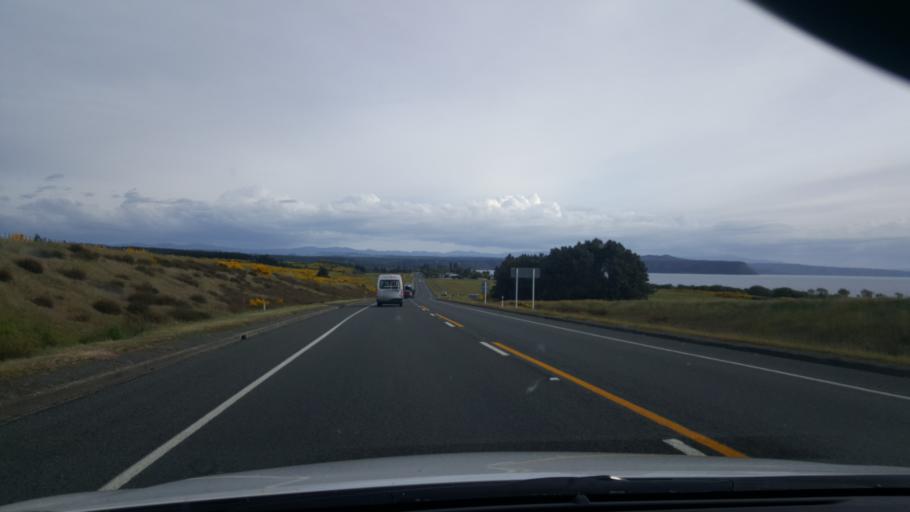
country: NZ
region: Waikato
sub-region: Taupo District
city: Taupo
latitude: -38.7429
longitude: 176.0731
